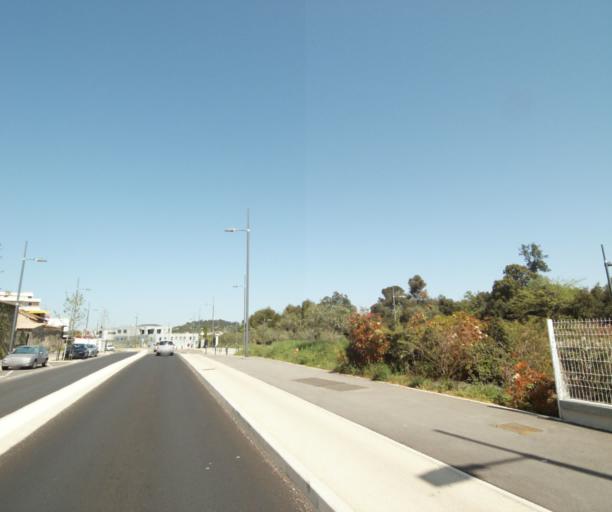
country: FR
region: Languedoc-Roussillon
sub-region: Departement de l'Herault
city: Castelnau-le-Lez
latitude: 43.6248
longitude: 3.9073
